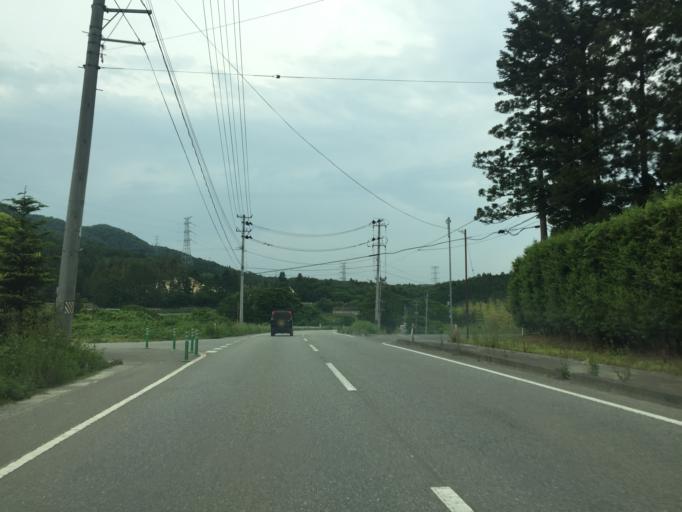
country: JP
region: Fukushima
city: Namie
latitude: 37.3852
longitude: 140.9567
